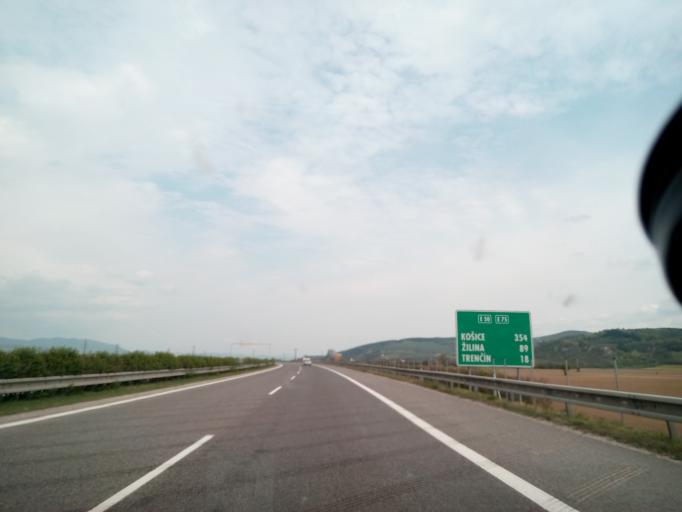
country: SK
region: Trenciansky
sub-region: Okres Nove Mesto nad Vahom
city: Nove Mesto nad Vahom
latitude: 48.7671
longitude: 17.8728
